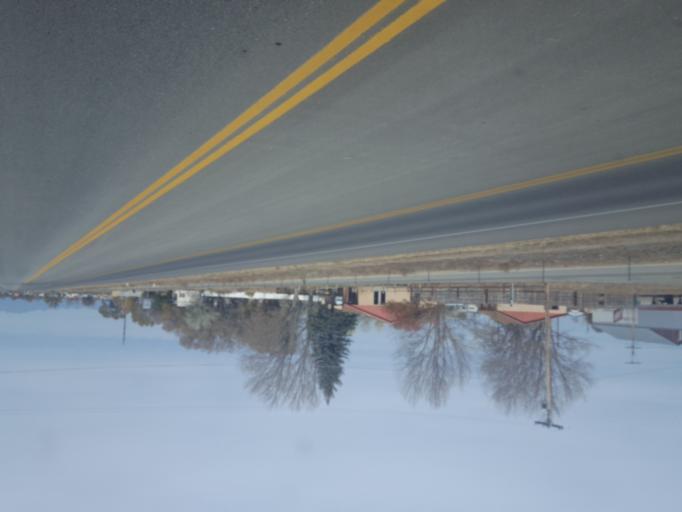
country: US
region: Colorado
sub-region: Alamosa County
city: Alamosa
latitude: 37.4486
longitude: -105.8810
